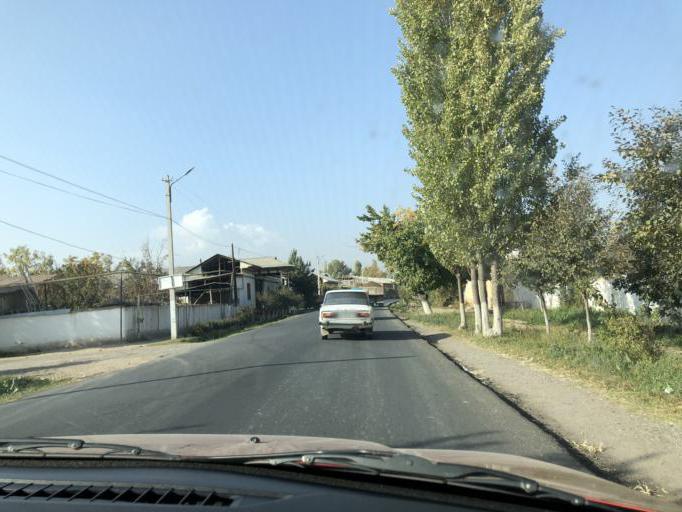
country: UZ
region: Namangan
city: Chust Shahri
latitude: 41.0669
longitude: 71.2052
